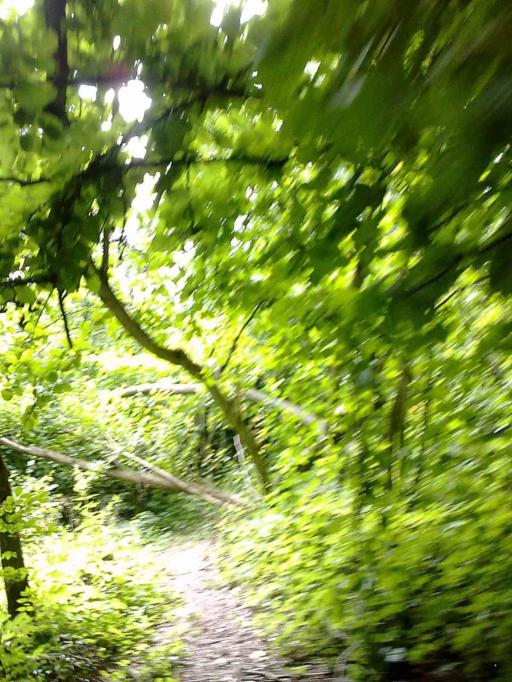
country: RU
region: Moskovskaya
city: Filimonki
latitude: 55.5639
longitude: 37.3761
